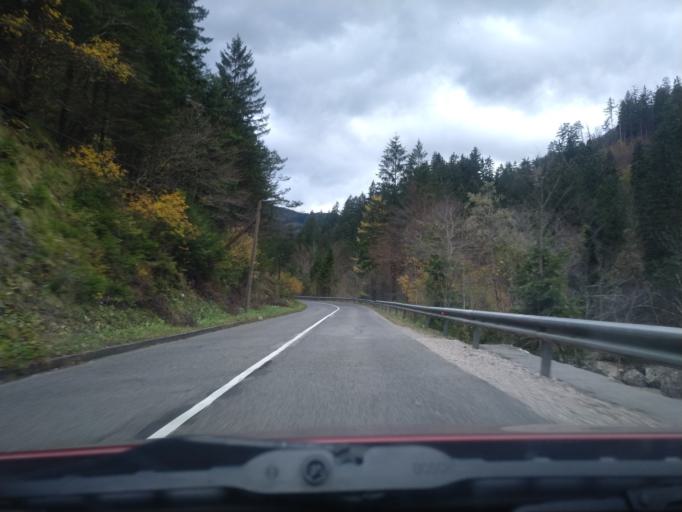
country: SI
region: Luce
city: Luce
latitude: 46.3834
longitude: 14.7251
